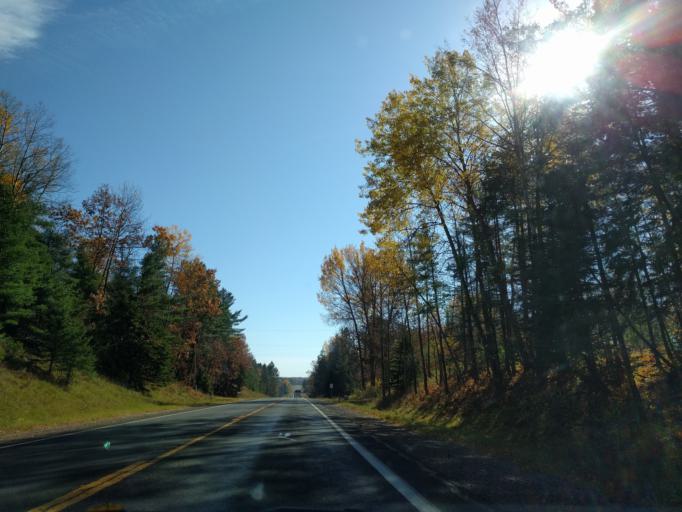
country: US
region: Michigan
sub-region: Iron County
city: Crystal Falls
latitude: 46.2534
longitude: -88.0117
